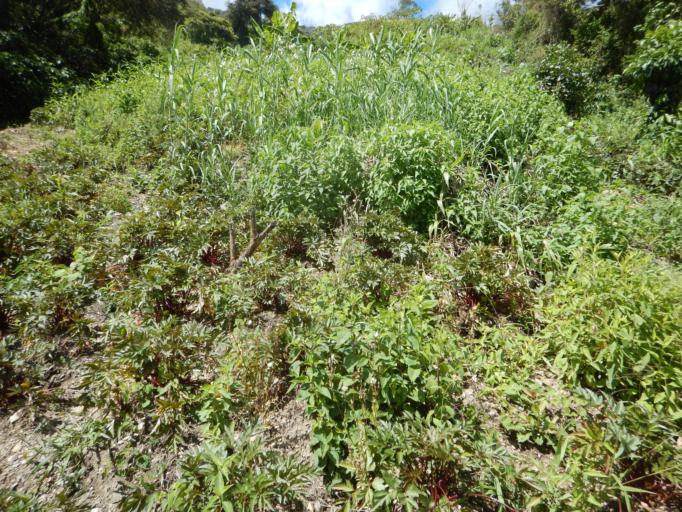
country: BO
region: La Paz
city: Coroico
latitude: -16.2792
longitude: -67.7119
